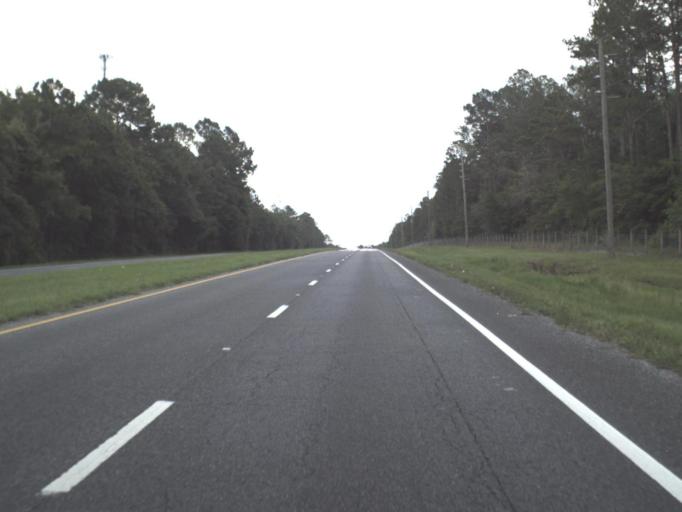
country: US
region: Florida
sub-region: Clay County
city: Middleburg
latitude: 29.9818
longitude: -81.9452
